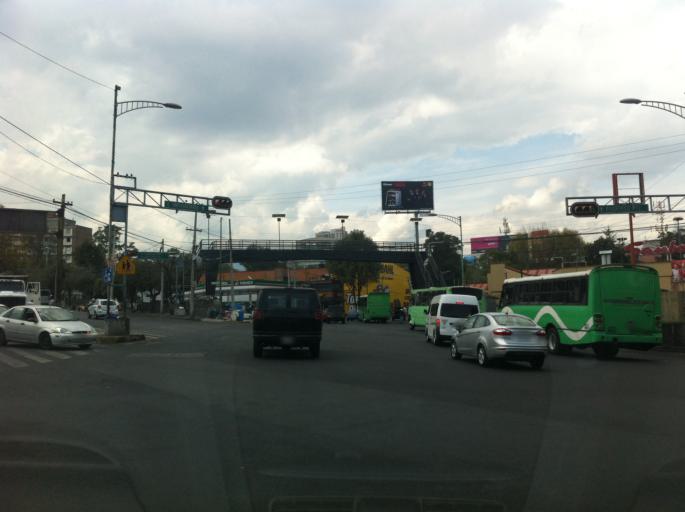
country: MX
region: Mexico City
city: Magdalena Contreras
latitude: 19.3387
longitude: -99.1921
